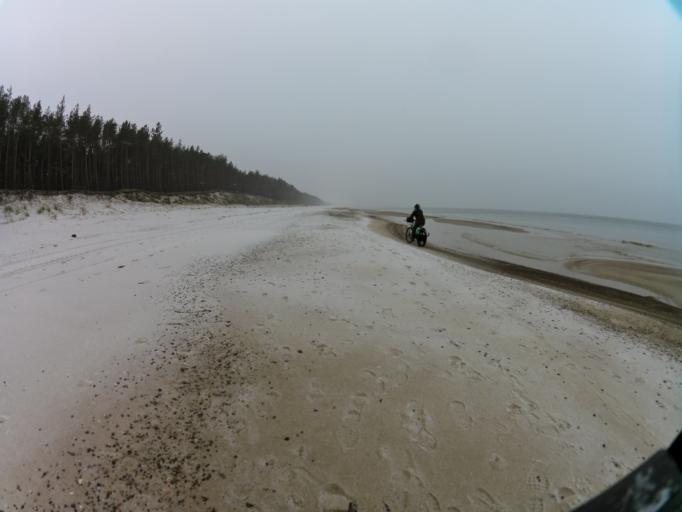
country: PL
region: West Pomeranian Voivodeship
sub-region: Powiat gryficki
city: Cerkwica
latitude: 54.1109
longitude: 15.1398
